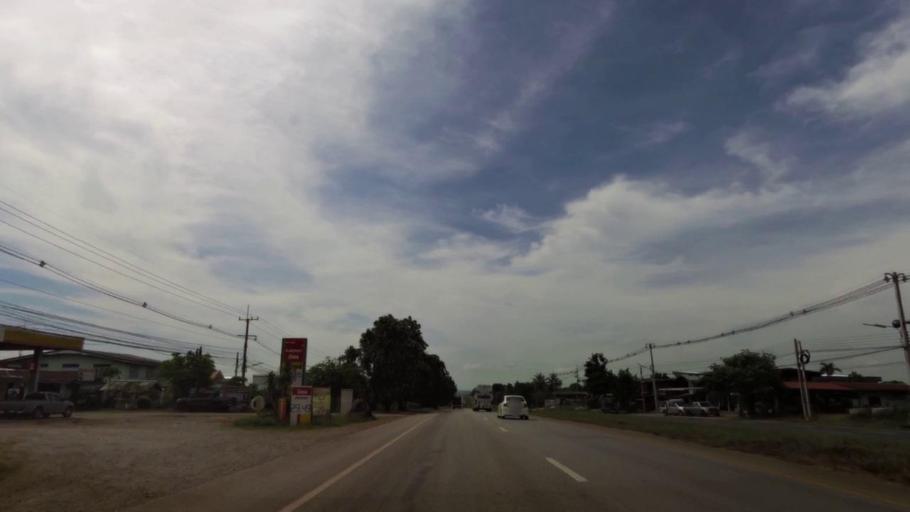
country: TH
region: Lop Buri
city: Chai Badan
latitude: 15.2382
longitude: 101.1251
